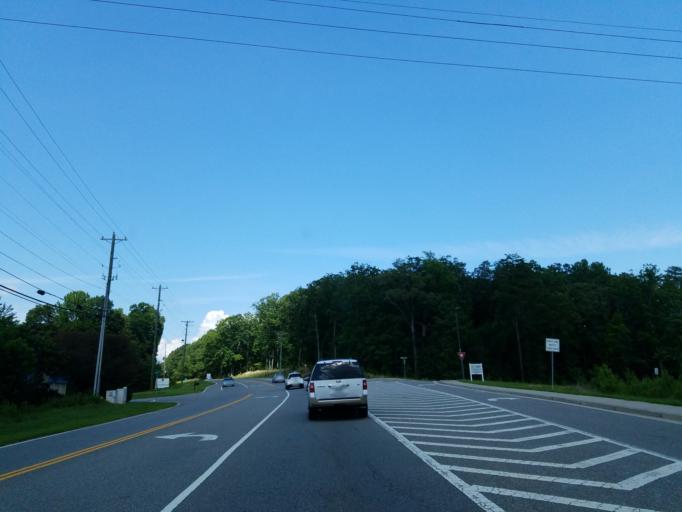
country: US
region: Georgia
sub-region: Forsyth County
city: Cumming
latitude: 34.2268
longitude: -84.1100
